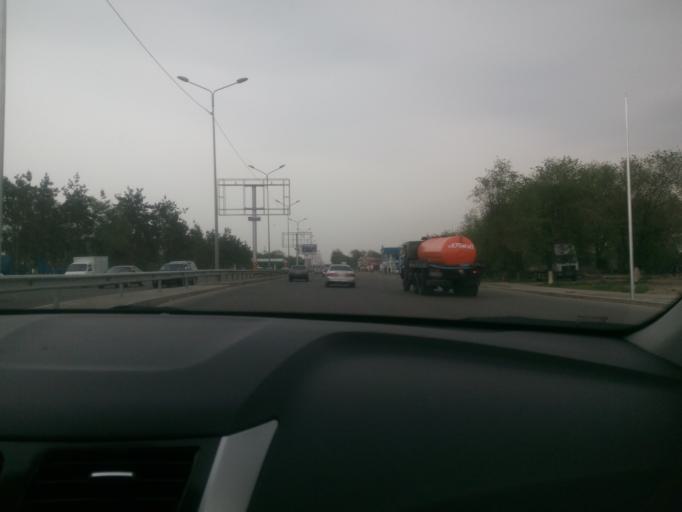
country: KZ
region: Almaty Qalasy
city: Almaty
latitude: 43.2362
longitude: 76.8050
